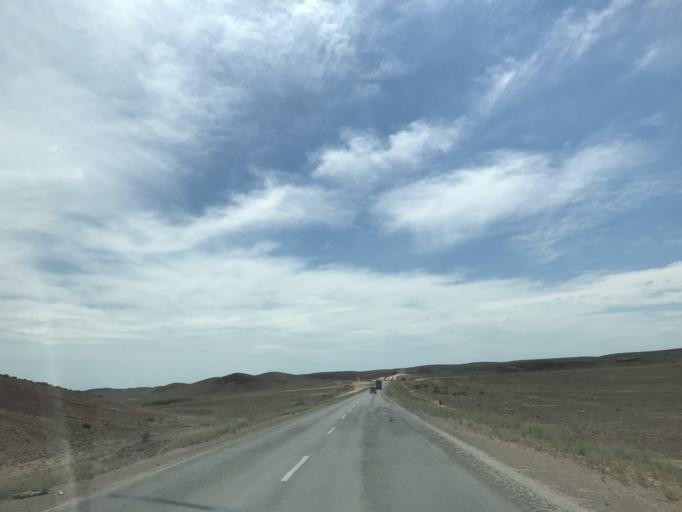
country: KZ
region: Almaty Oblysy
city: Ulken
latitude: 45.0726
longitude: 73.9888
